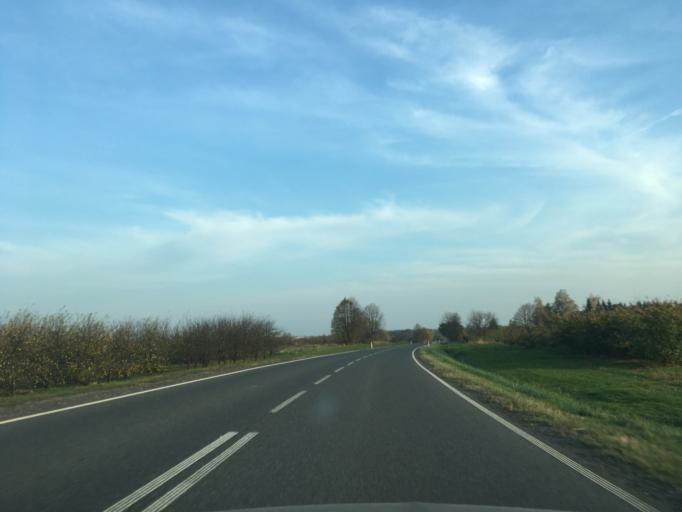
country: PL
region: Lodz Voivodeship
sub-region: Powiat skierniewicki
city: Kowiesy
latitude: 51.9233
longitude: 20.4250
